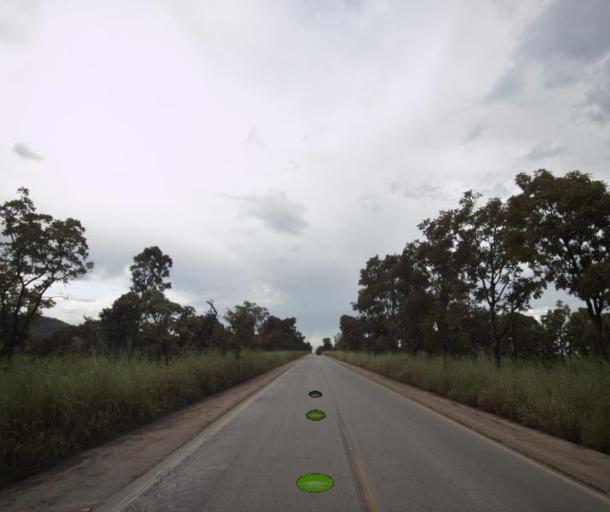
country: BR
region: Goias
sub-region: Porangatu
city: Porangatu
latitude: -13.6120
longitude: -49.0423
